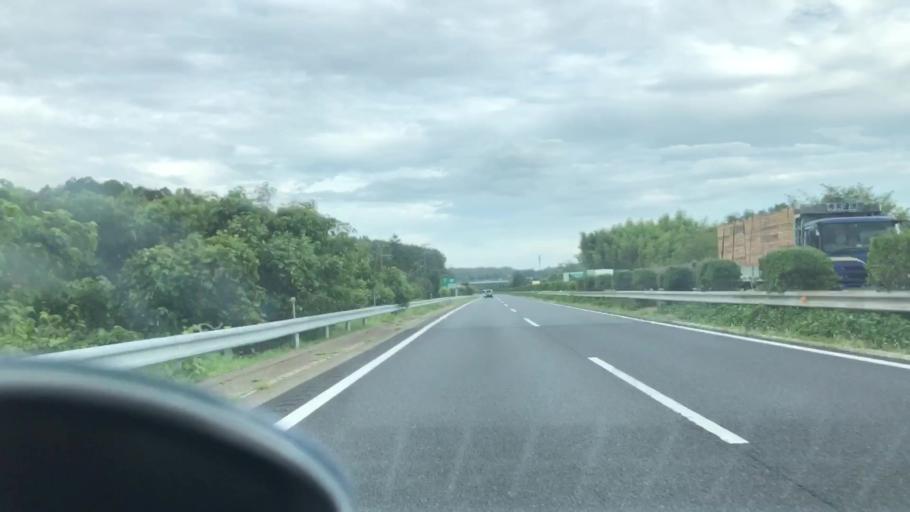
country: JP
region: Hyogo
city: Yashiro
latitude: 34.9249
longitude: 134.9883
